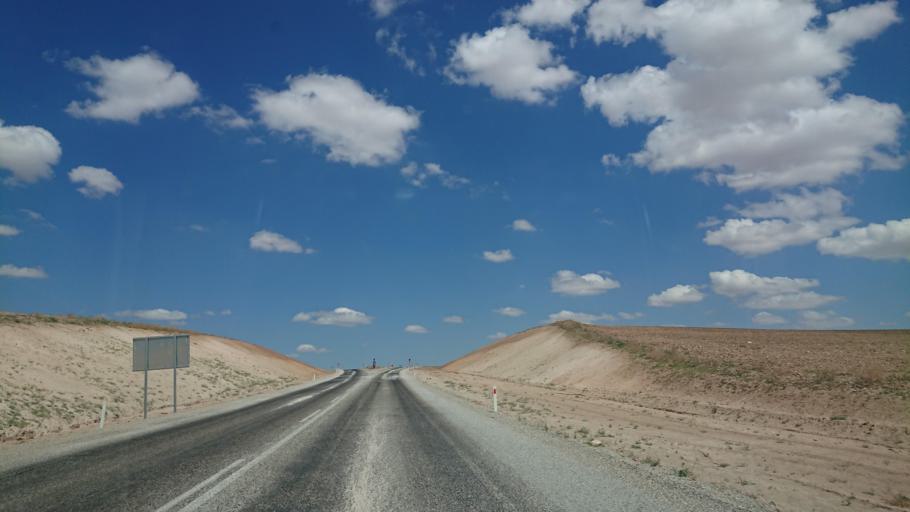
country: TR
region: Aksaray
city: Sariyahsi
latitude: 39.1232
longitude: 33.9661
